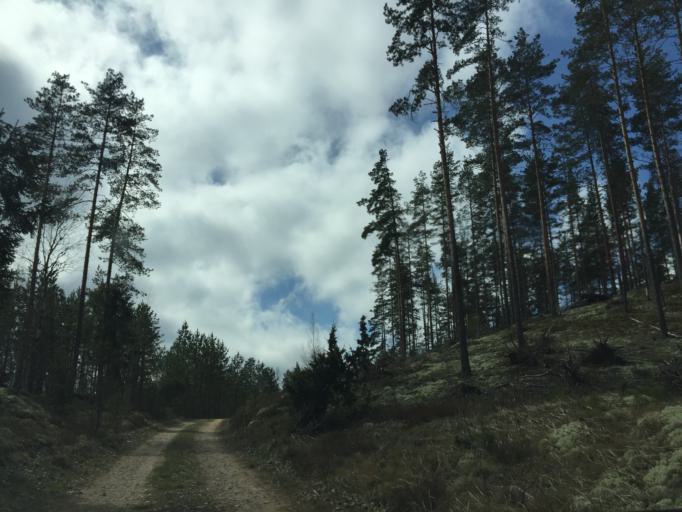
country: EE
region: Valgamaa
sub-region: Valga linn
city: Valga
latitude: 57.6263
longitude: 26.2321
